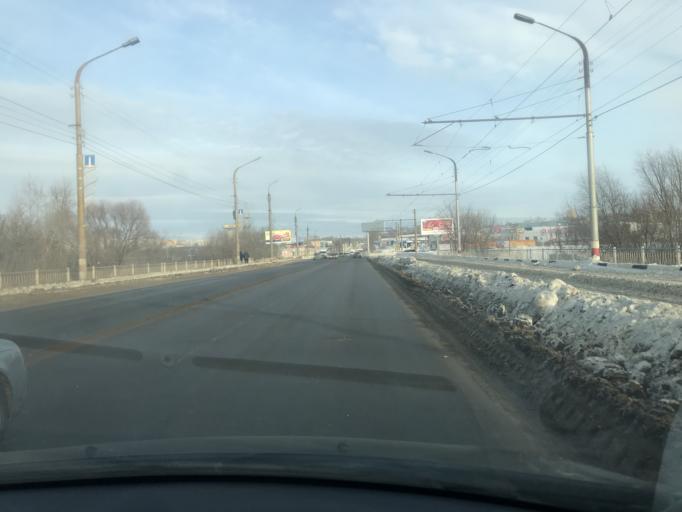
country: RU
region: Ulyanovsk
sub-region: Ulyanovskiy Rayon
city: Ulyanovsk
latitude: 54.3250
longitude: 48.3572
